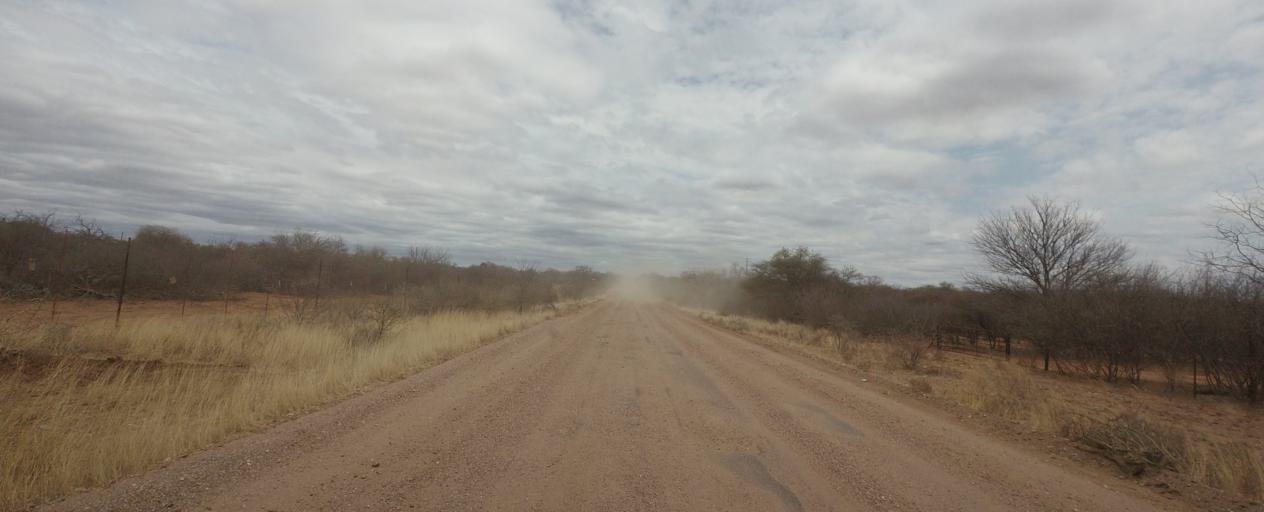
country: BW
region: Central
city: Mathathane
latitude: -22.6757
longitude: 28.6717
